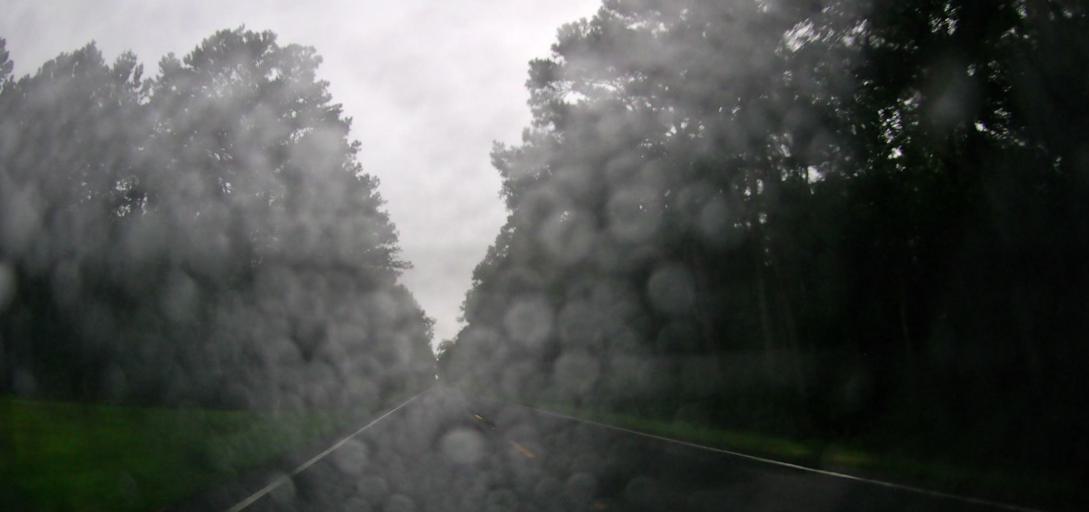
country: US
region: Georgia
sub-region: Glynn County
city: Dock Junction
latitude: 31.2847
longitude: -81.6737
